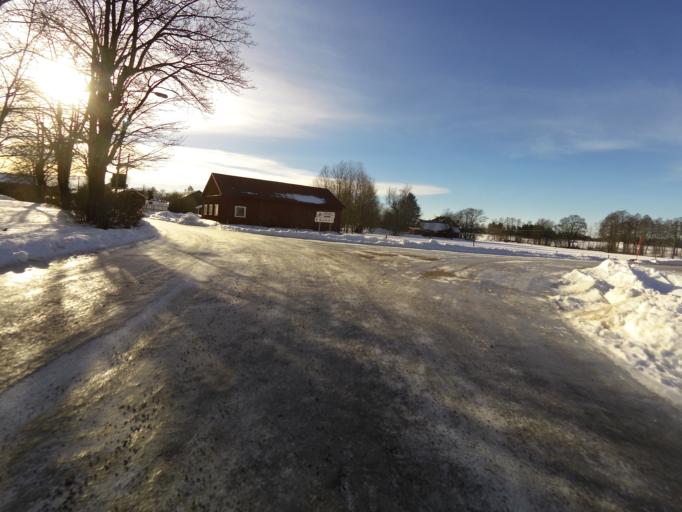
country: SE
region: Gaevleborg
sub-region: Gavle Kommun
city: Valbo
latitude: 60.6539
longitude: 17.0664
